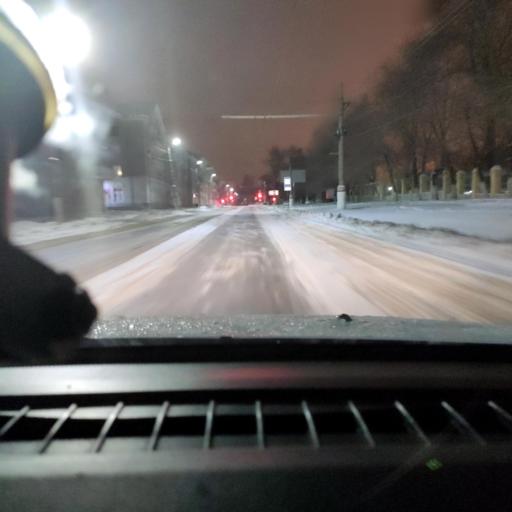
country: RU
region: Samara
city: Novokuybyshevsk
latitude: 53.1027
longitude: 49.9457
